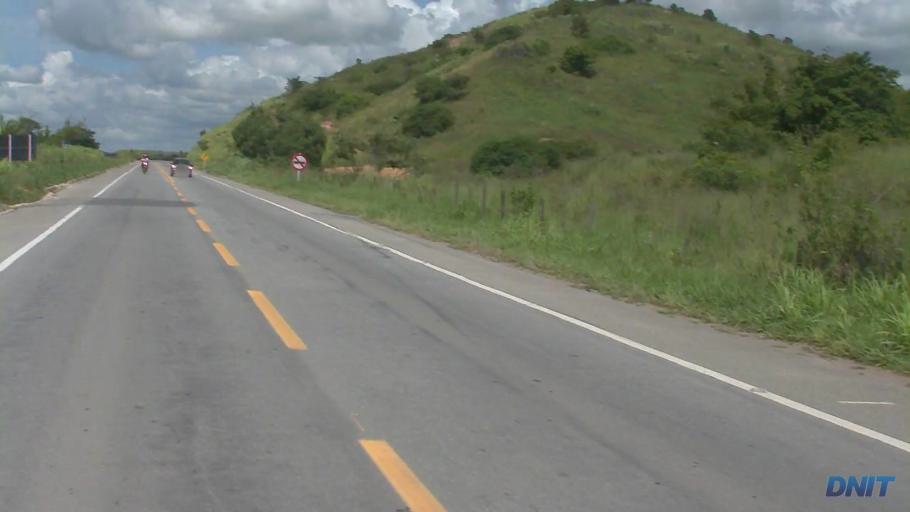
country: BR
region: Minas Gerais
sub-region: Governador Valadares
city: Governador Valadares
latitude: -18.9714
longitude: -42.0940
